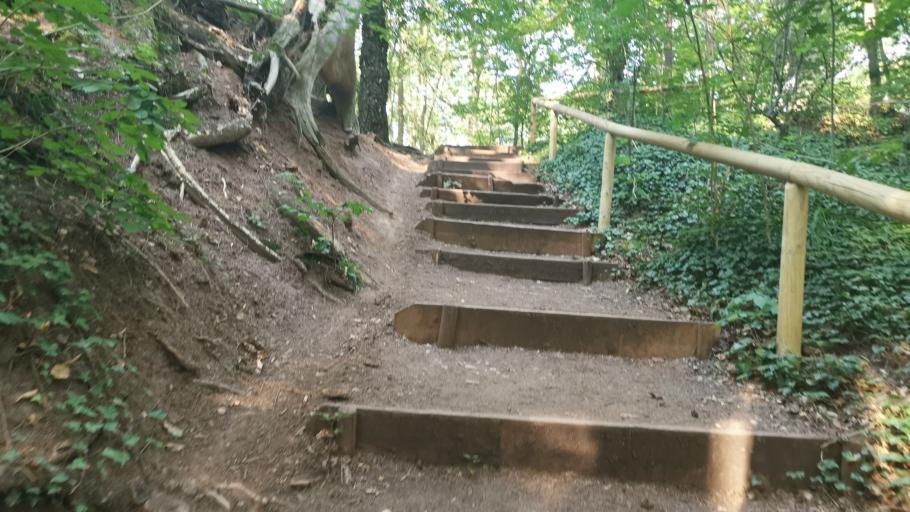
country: DE
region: Bavaria
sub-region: Regierungsbezirk Mittelfranken
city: Schwaig
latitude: 49.4495
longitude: 11.1477
